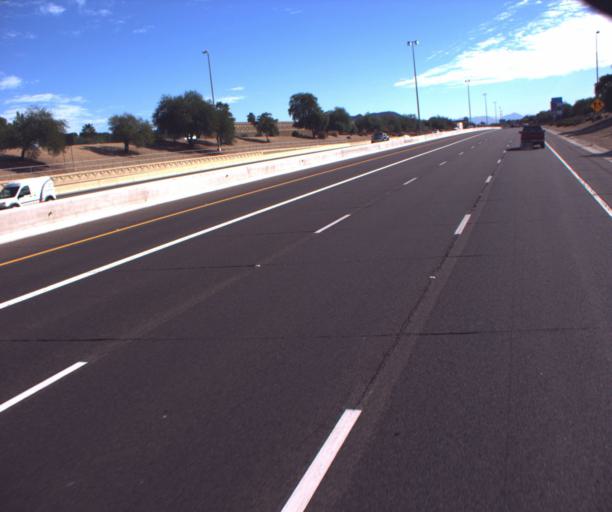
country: US
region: Arizona
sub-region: Maricopa County
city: Sun City
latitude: 33.6677
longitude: -112.2188
